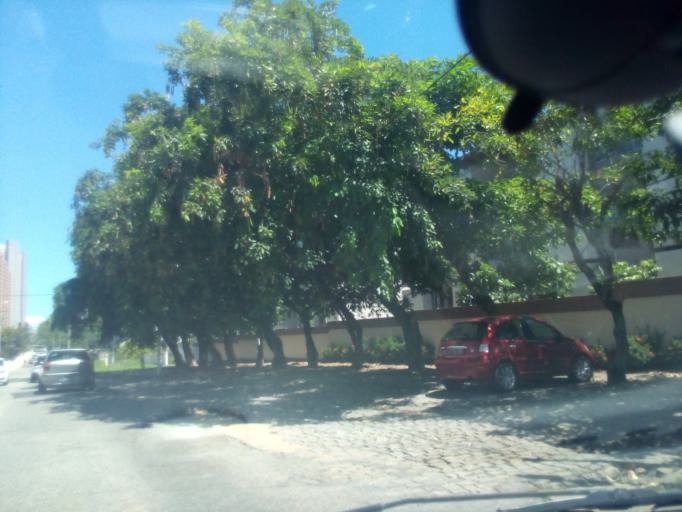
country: BR
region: Rio Grande do Norte
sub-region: Natal
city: Natal
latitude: -5.8447
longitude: -35.2151
